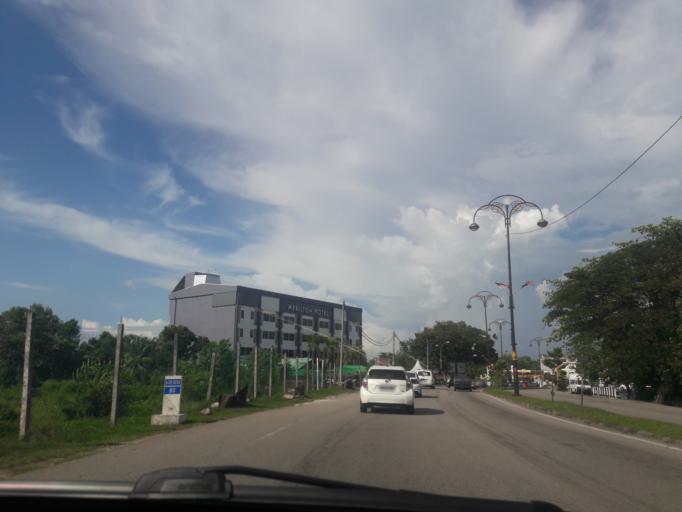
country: MY
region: Kedah
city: Sungai Petani
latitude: 5.6347
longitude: 100.4840
